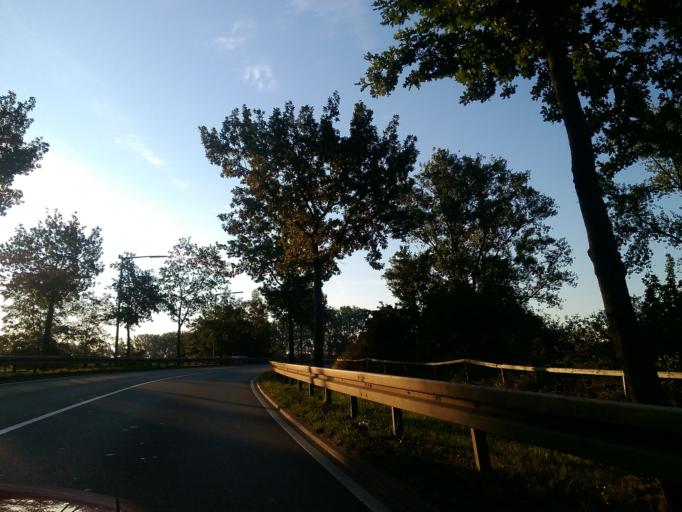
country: DE
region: Baden-Wuerttemberg
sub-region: Karlsruhe Region
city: Karlsruhe
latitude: 48.9995
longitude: 8.4292
